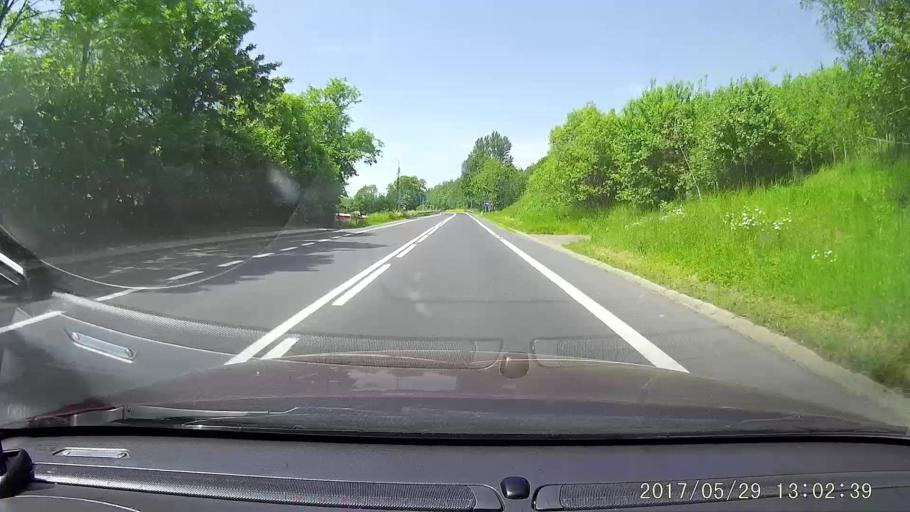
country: PL
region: Lower Silesian Voivodeship
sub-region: Powiat jeleniogorski
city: Stara Kamienica
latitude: 50.9161
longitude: 15.6251
